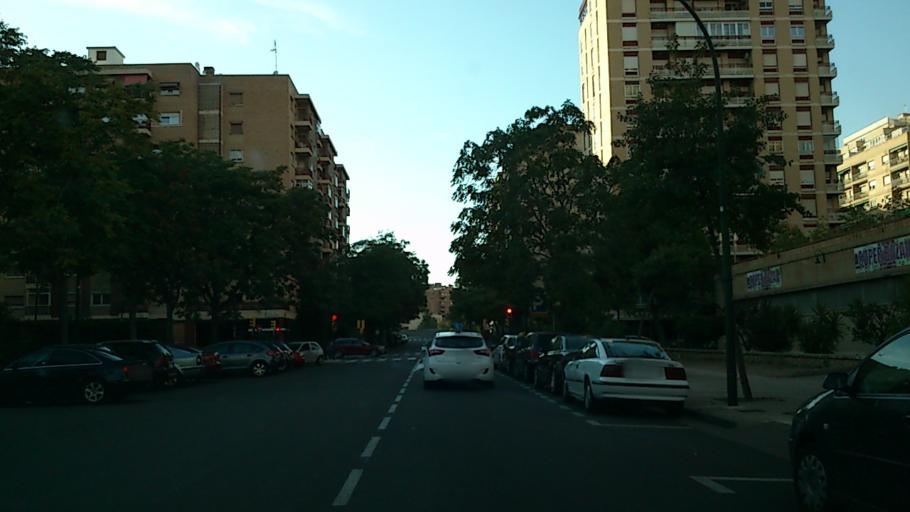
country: ES
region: Aragon
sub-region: Provincia de Zaragoza
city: Delicias
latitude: 41.6346
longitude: -0.9059
